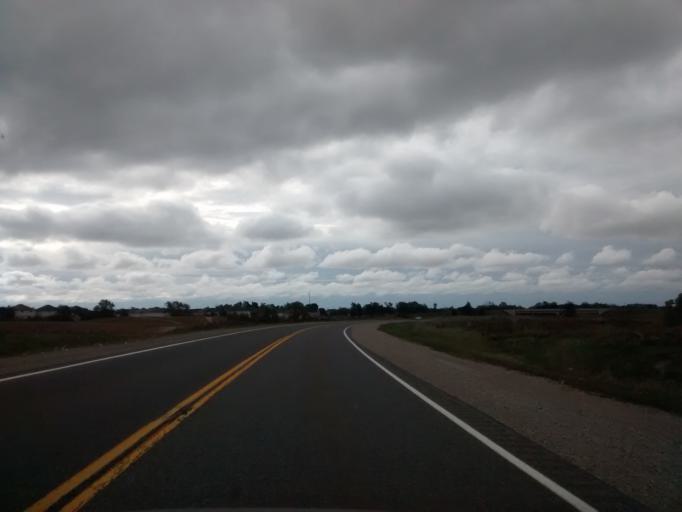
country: CA
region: Ontario
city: Ancaster
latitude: 43.1520
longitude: -79.9280
